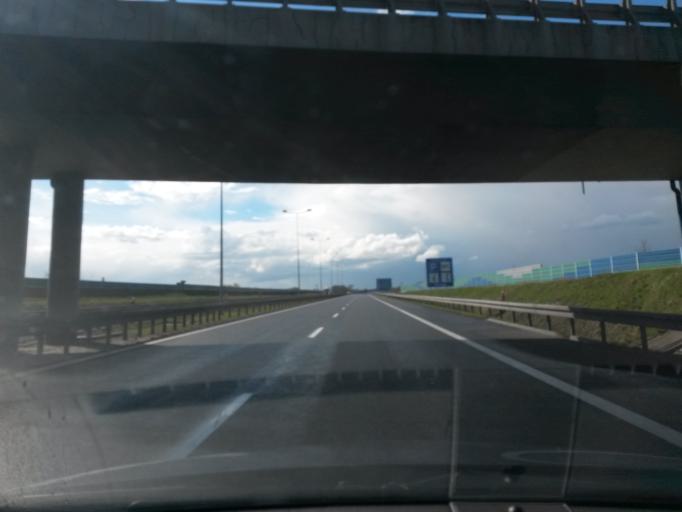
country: PL
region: Greater Poland Voivodeship
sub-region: Powiat wrzesinski
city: Wrzesnia
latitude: 52.3098
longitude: 17.5735
